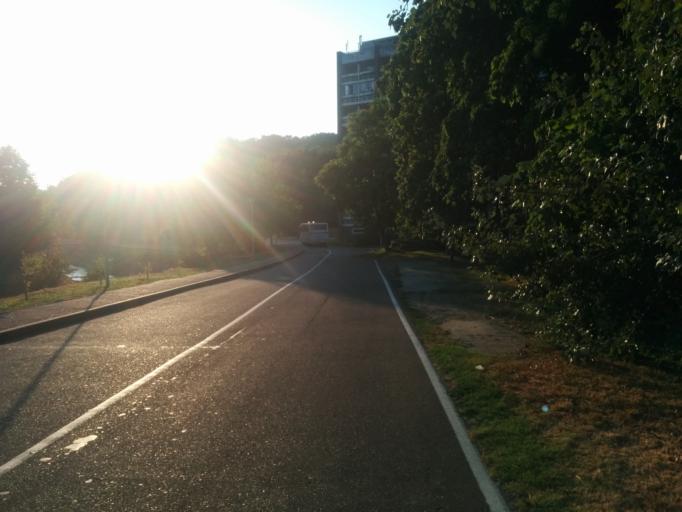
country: RU
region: Krasnodarskiy
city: Novomikhaylovskiy
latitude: 44.2596
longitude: 38.8218
